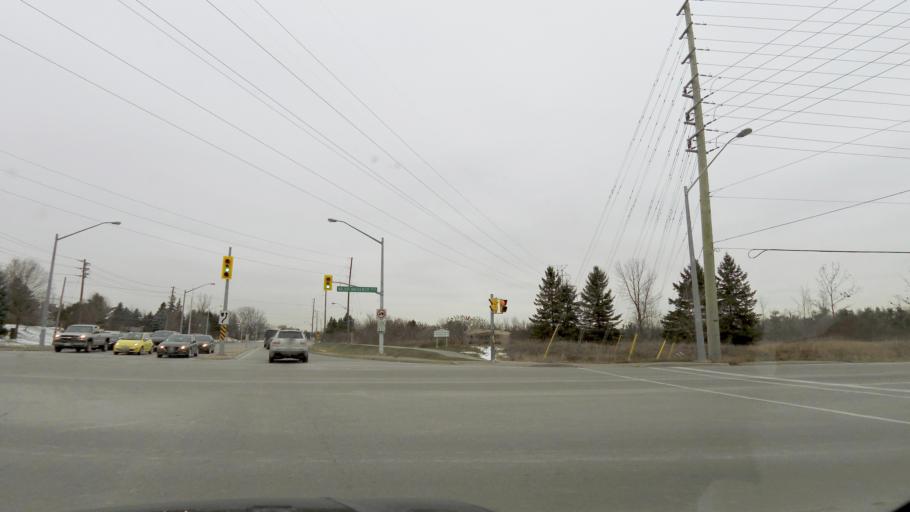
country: CA
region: Ontario
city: Vaughan
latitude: 43.8324
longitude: -79.6174
